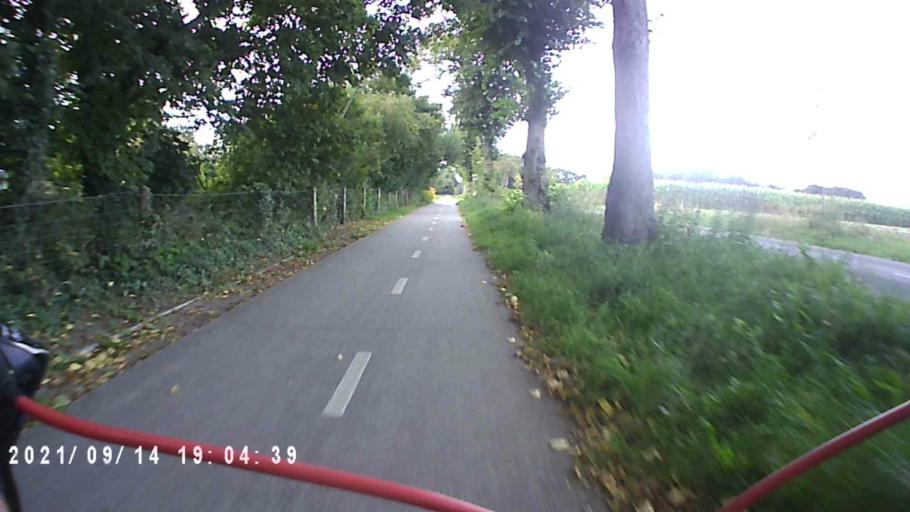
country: NL
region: Drenthe
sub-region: Gemeente Aa en Hunze
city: Anloo
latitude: 53.0424
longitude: 6.7324
